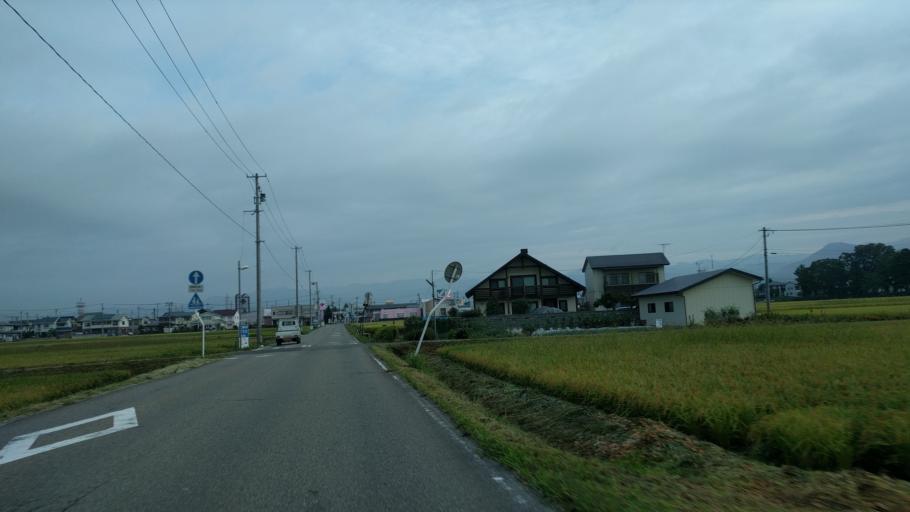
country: JP
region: Fukushima
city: Kitakata
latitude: 37.6434
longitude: 139.8807
